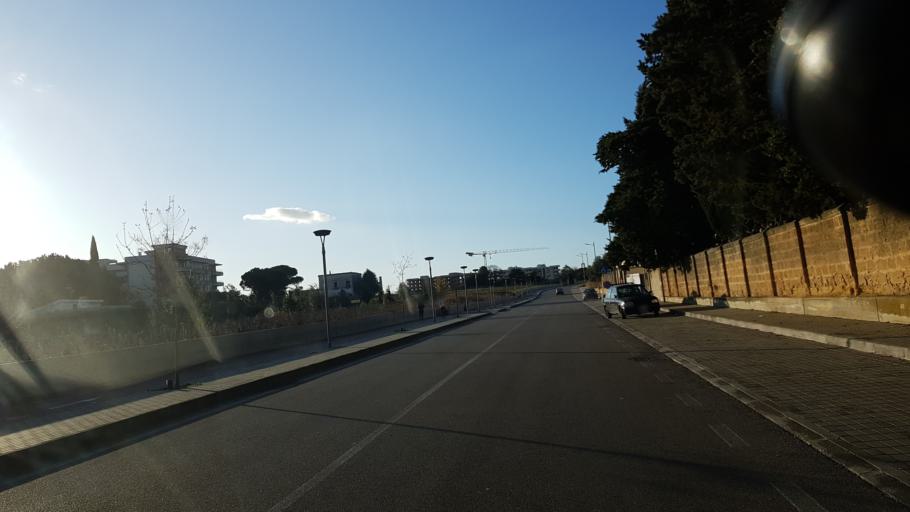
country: IT
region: Apulia
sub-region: Provincia di Bari
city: Gioia del Colle
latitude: 40.8012
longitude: 16.9119
